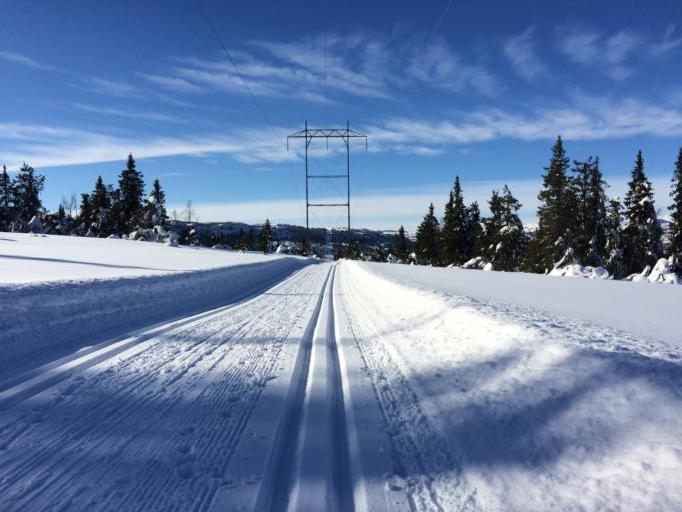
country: NO
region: Oppland
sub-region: Gausdal
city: Segalstad bru
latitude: 61.3157
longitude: 10.1006
